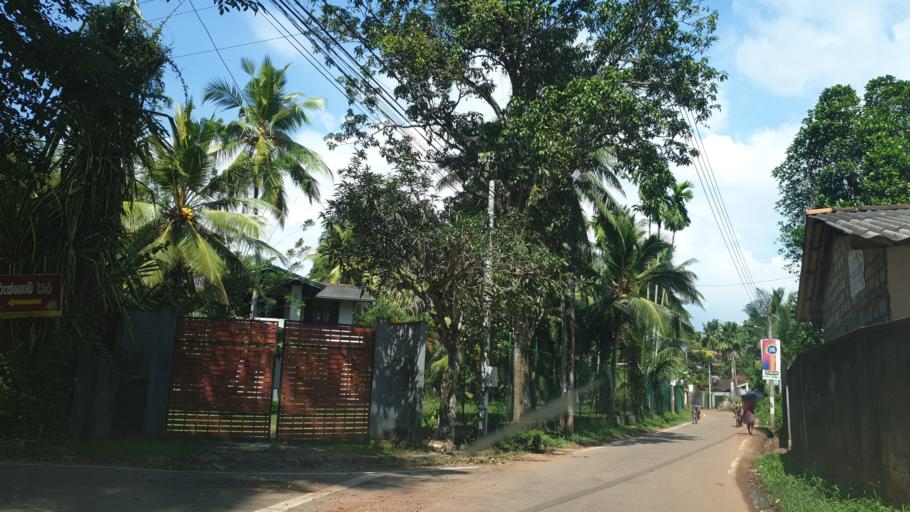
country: LK
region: Western
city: Panadura
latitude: 6.7093
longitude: 79.9587
